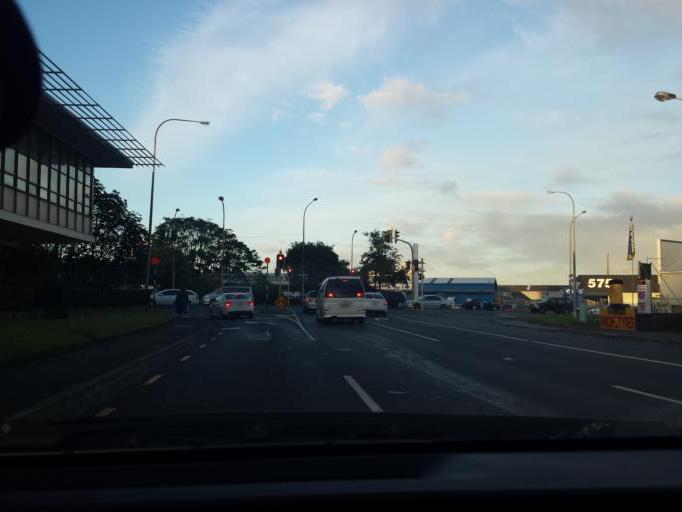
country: NZ
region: Auckland
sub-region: Auckland
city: Tamaki
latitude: -36.9109
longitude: 174.8187
